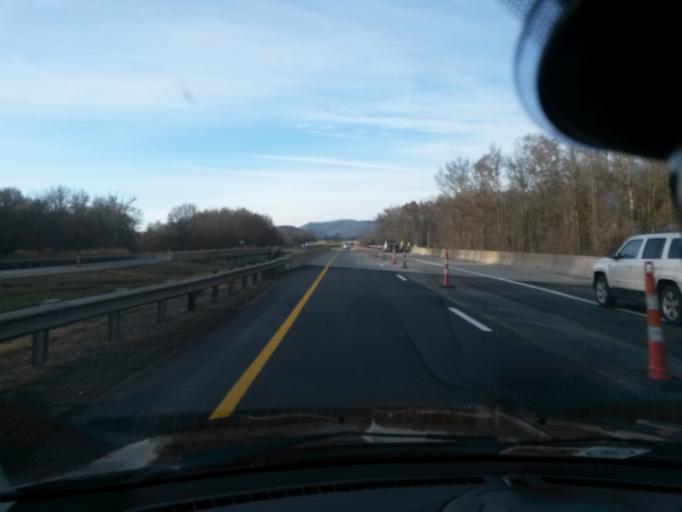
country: US
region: West Virginia
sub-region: Greenbrier County
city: Rainelle
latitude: 37.8617
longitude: -80.7146
